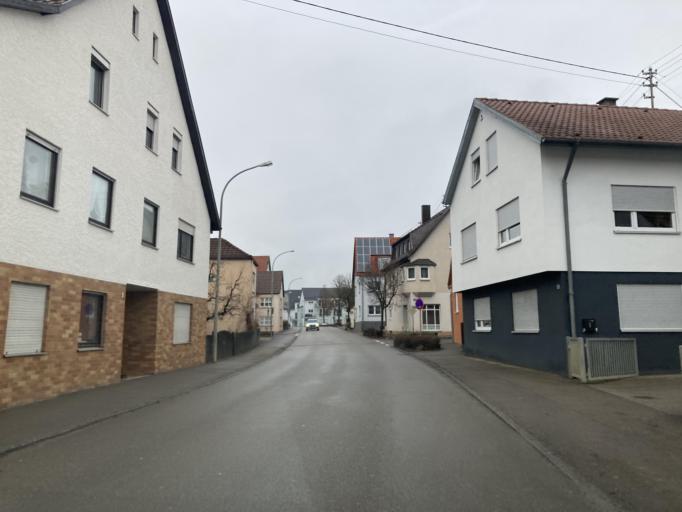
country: DE
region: Baden-Wuerttemberg
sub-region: Regierungsbezirk Stuttgart
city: Sontheim an der Brenz
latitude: 48.5629
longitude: 10.2953
